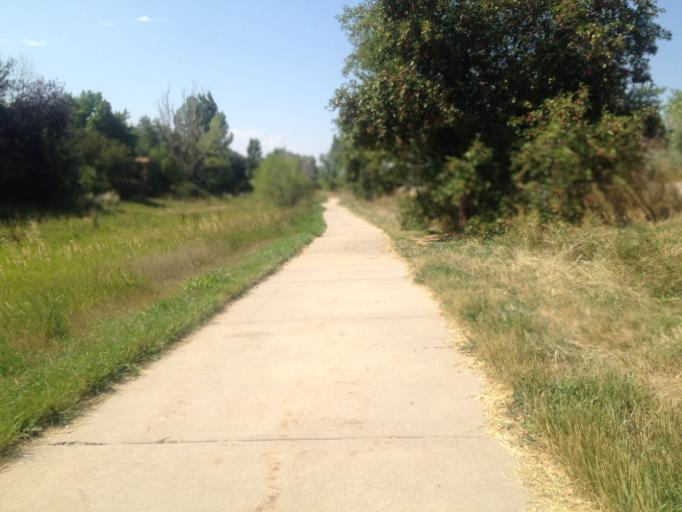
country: US
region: Colorado
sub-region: Boulder County
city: Louisville
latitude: 39.9950
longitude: -105.1383
